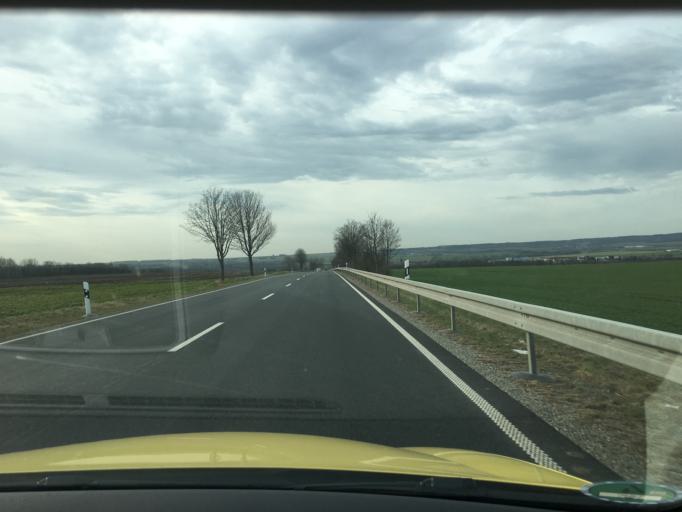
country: DE
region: Thuringia
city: Buttelstedt
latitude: 51.0908
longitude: 11.3485
